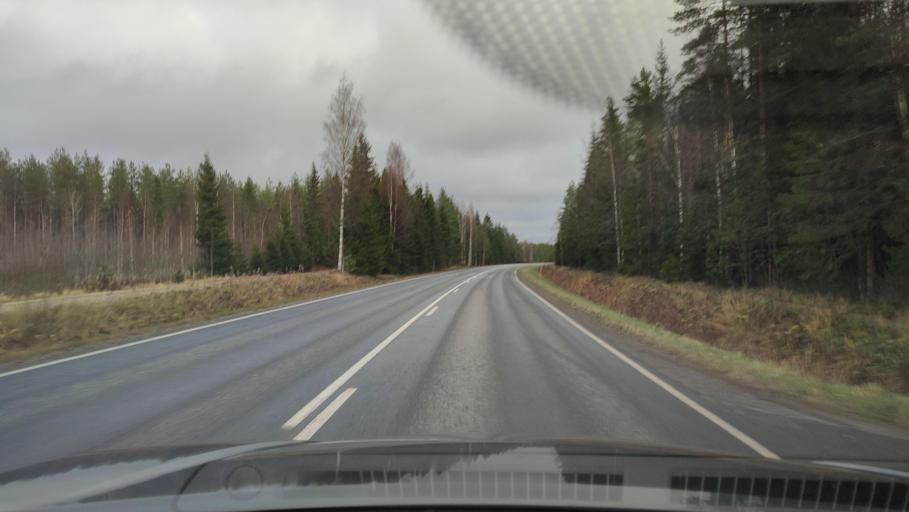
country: FI
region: Southern Ostrobothnia
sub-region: Suupohja
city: Kauhajoki
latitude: 62.3899
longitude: 22.1453
